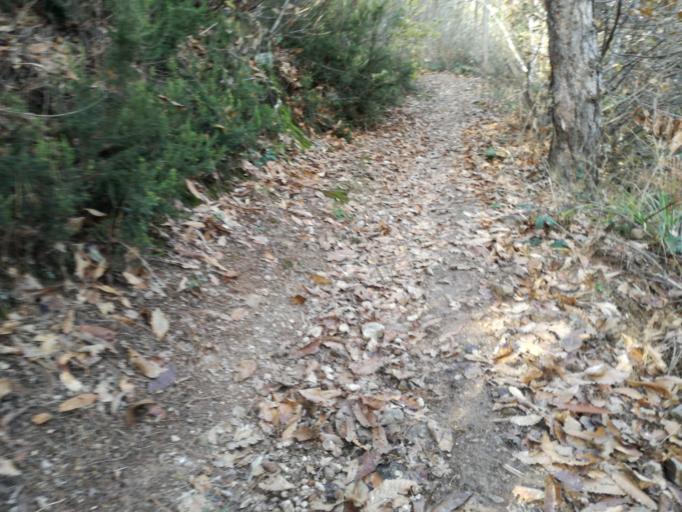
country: IT
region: Veneto
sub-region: Provincia di Padova
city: Arqua Petrarca
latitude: 45.2797
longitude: 11.7207
